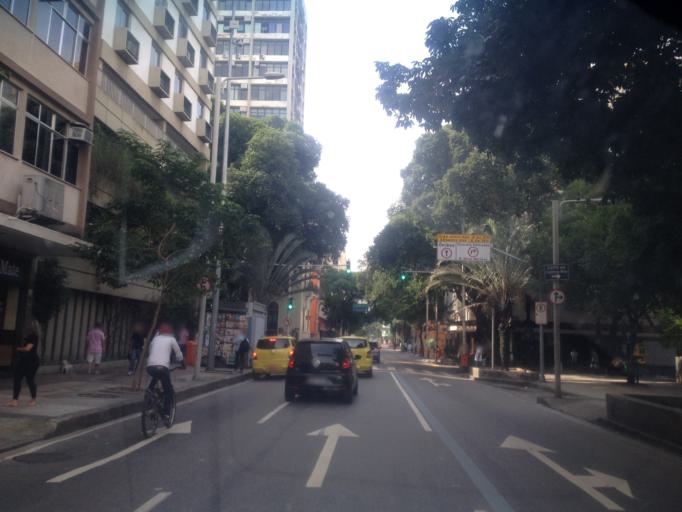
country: BR
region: Rio de Janeiro
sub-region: Rio De Janeiro
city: Rio de Janeiro
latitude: -22.9531
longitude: -43.1891
